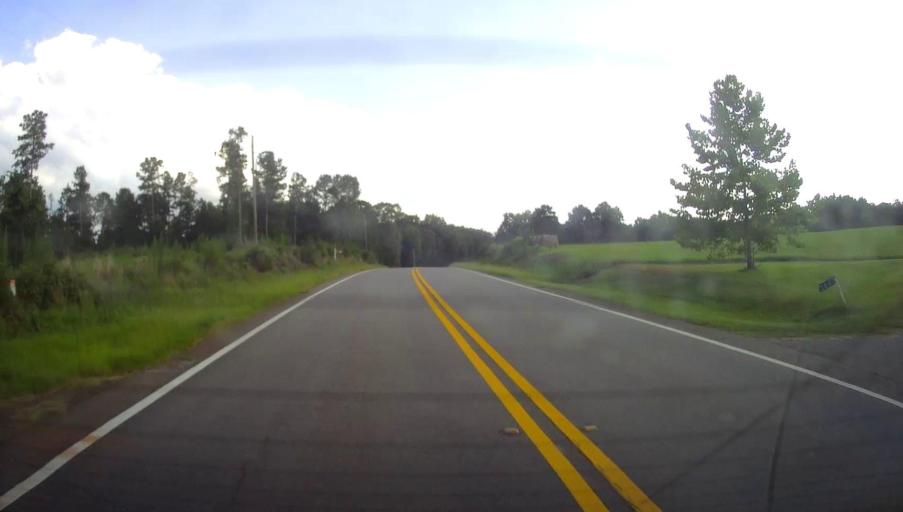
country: US
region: Georgia
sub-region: Monroe County
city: Forsyth
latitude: 32.9347
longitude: -83.9606
